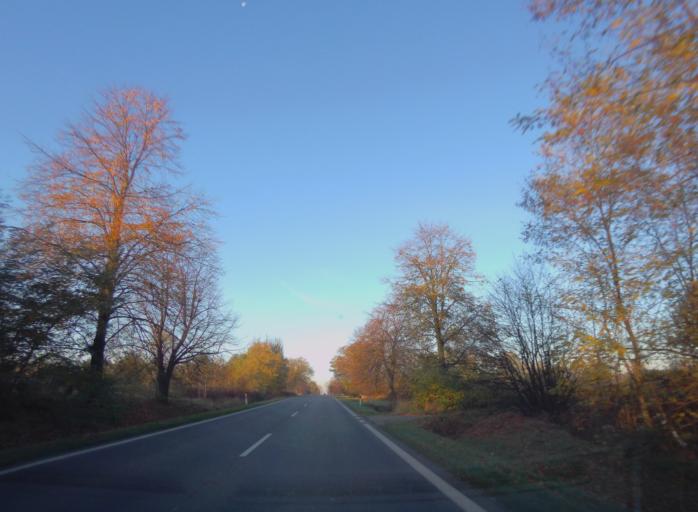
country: PL
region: Subcarpathian Voivodeship
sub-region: Powiat rzeszowski
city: Wolka Niedzwiedzka
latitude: 50.2471
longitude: 22.2089
